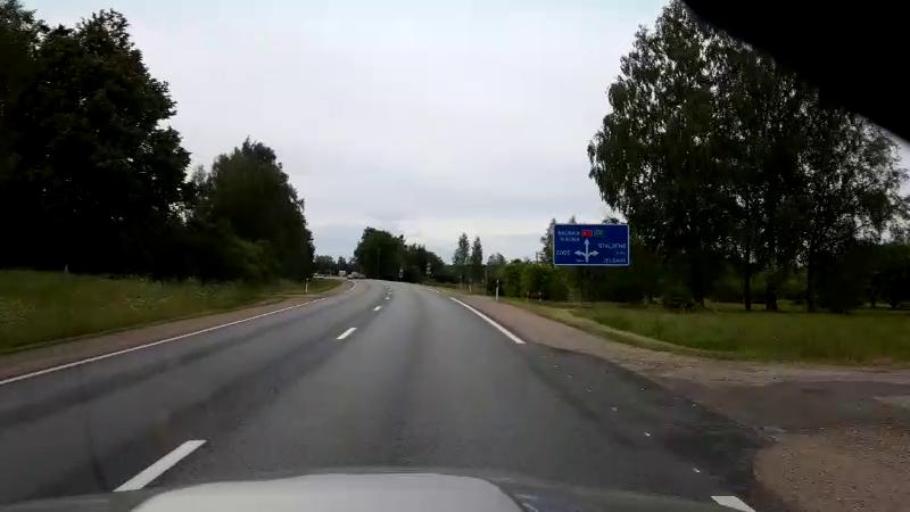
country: LV
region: Bauskas Rajons
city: Bauska
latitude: 56.4668
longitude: 24.1633
